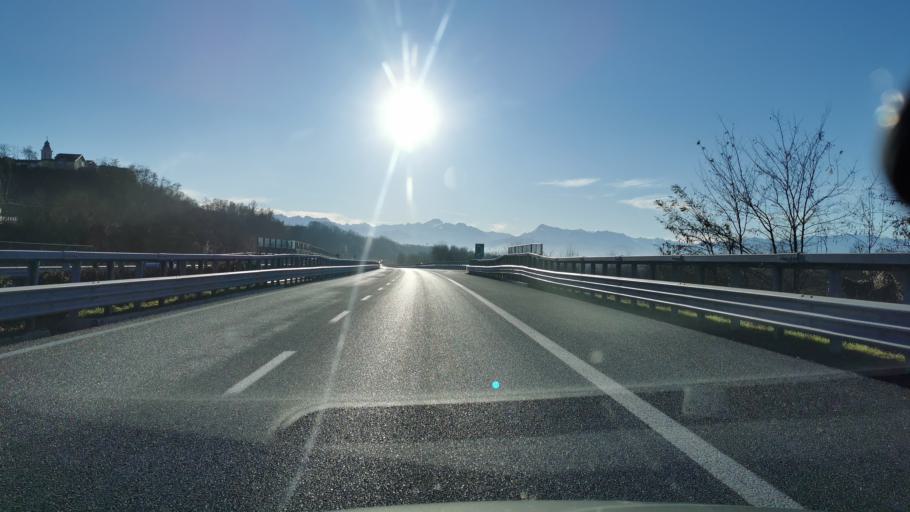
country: IT
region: Piedmont
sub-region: Provincia di Cuneo
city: Montanera
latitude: 44.4678
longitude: 7.6672
